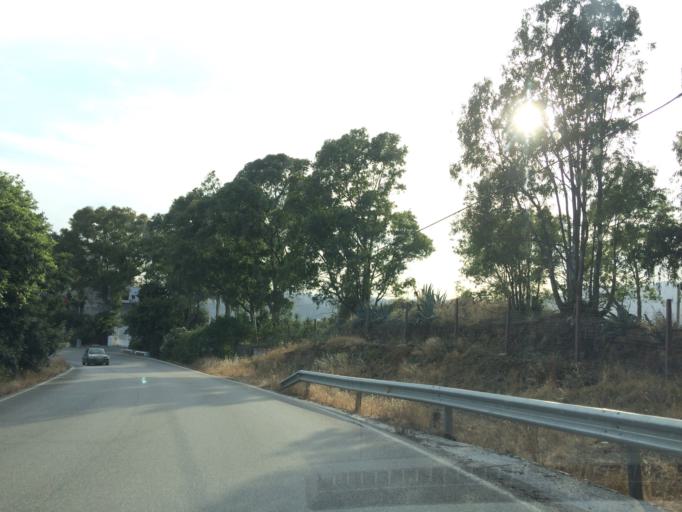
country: ES
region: Andalusia
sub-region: Provincia de Malaga
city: Malaga
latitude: 36.7459
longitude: -4.4099
